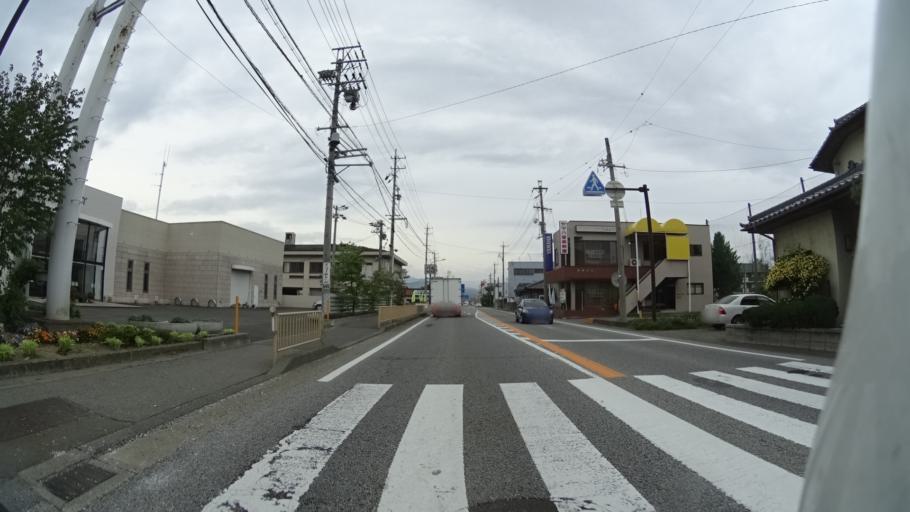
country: JP
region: Nagano
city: Nagano-shi
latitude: 36.5345
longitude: 138.1229
